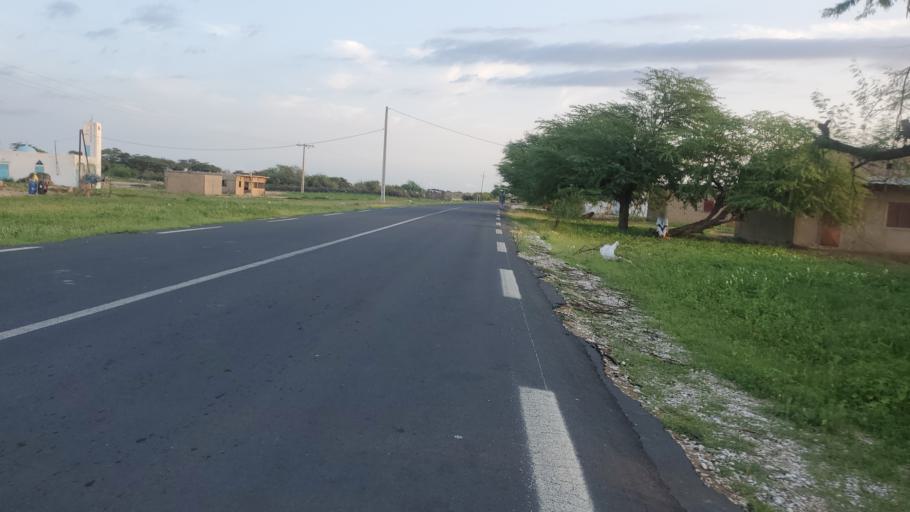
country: SN
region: Saint-Louis
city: Saint-Louis
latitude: 16.1424
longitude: -16.4097
